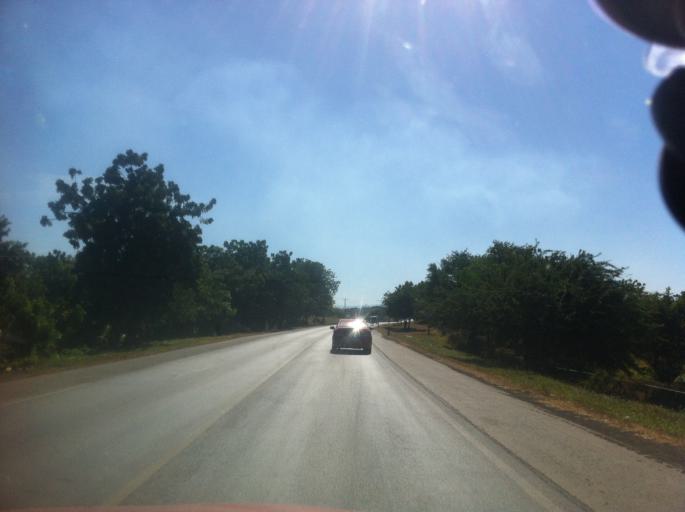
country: NI
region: Managua
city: Tipitapa
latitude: 12.2869
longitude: -86.0590
